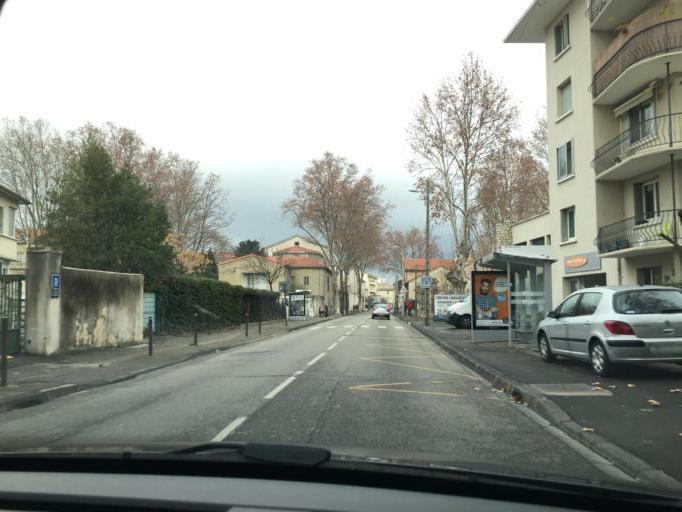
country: FR
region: Provence-Alpes-Cote d'Azur
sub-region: Departement du Vaucluse
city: Avignon
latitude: 43.9347
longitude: 4.8103
